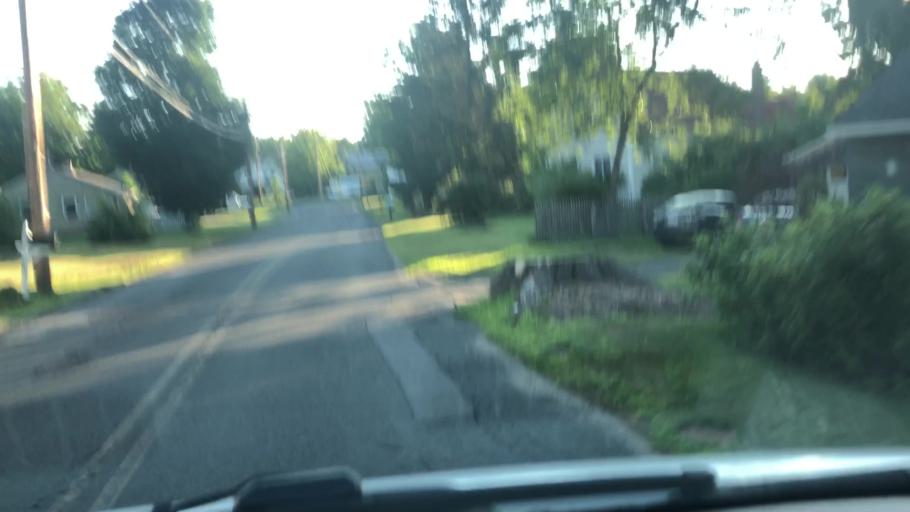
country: US
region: Massachusetts
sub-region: Hampshire County
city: Williamsburg
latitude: 42.3877
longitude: -72.7289
